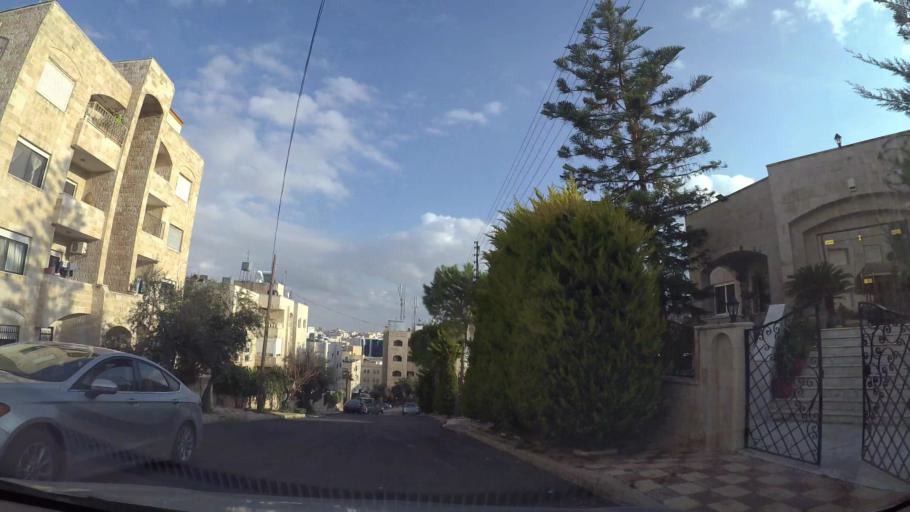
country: JO
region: Amman
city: Al Jubayhah
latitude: 32.0007
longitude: 35.8707
